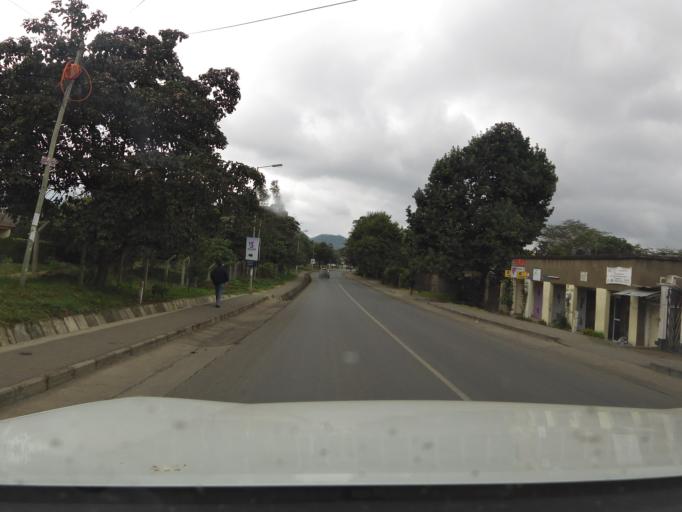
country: TZ
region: Arusha
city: Arusha
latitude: -3.3654
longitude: 36.6853
